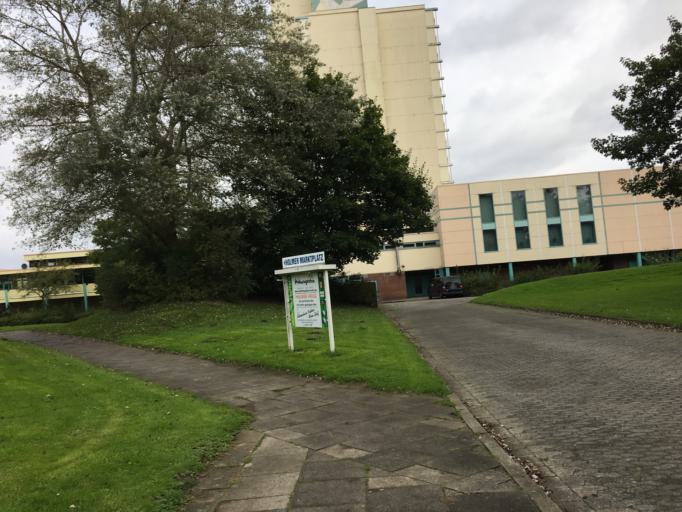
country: DE
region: Schleswig-Holstein
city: Wisch
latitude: 54.4219
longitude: 10.3697
